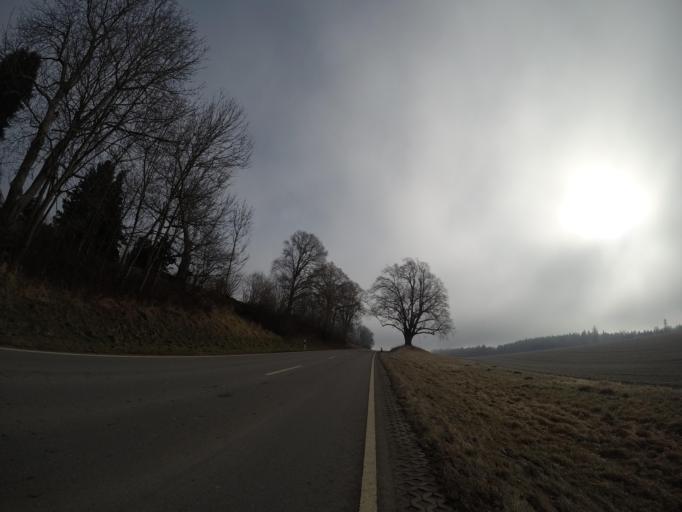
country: DE
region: Bavaria
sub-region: Swabia
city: Senden
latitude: 48.3487
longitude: 10.0501
